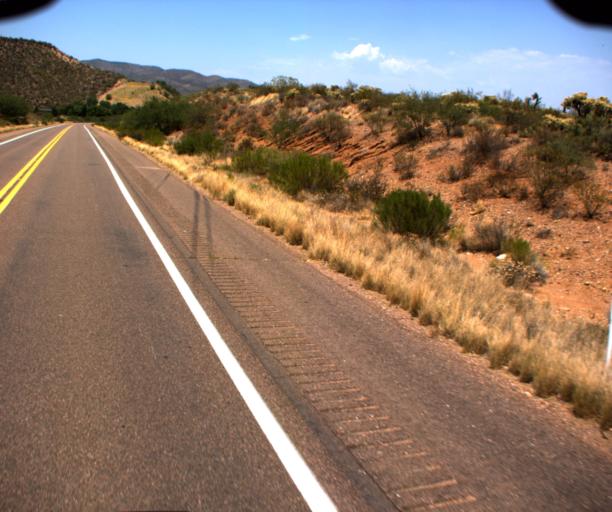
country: US
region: Arizona
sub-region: Gila County
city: Tonto Basin
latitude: 33.9357
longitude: -111.3150
